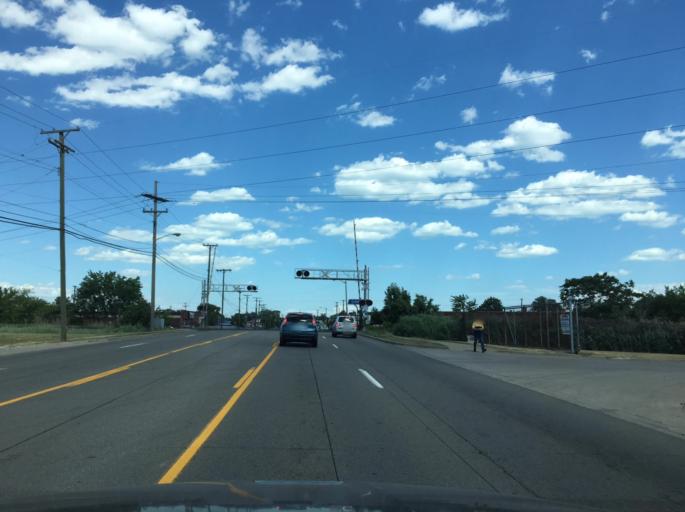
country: US
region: Michigan
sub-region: Macomb County
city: Roseville
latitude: 42.5090
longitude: -82.9616
